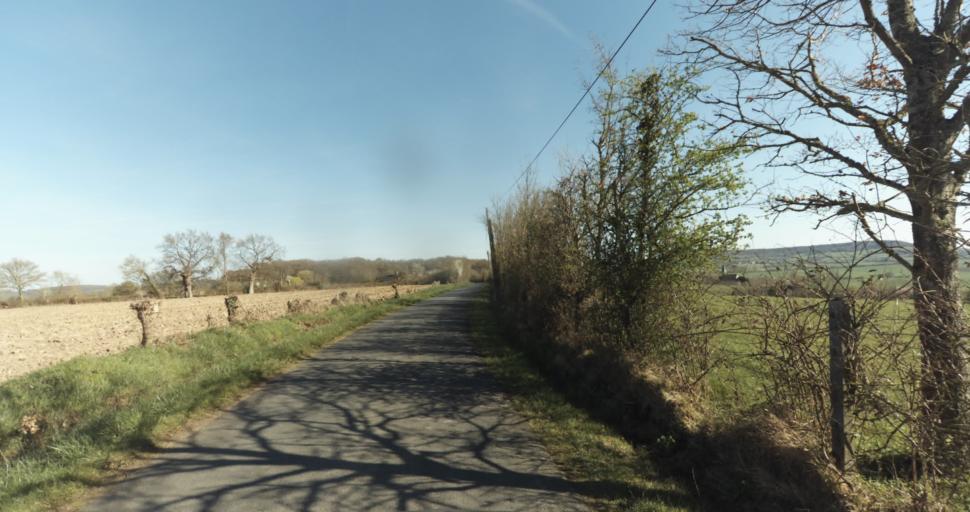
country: FR
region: Lower Normandy
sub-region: Departement du Calvados
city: Saint-Pierre-sur-Dives
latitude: 49.0450
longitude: 0.0355
